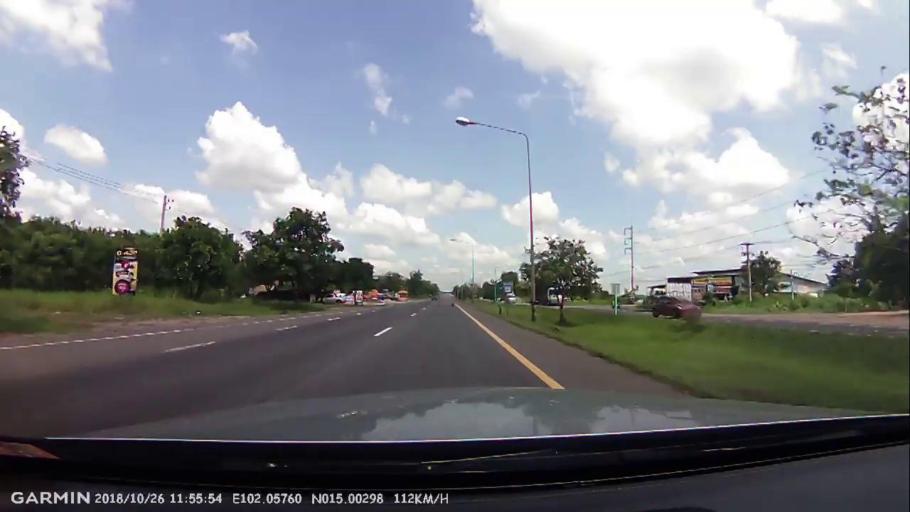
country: TH
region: Nakhon Ratchasima
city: Nakhon Ratchasima
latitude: 15.0031
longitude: 102.0576
